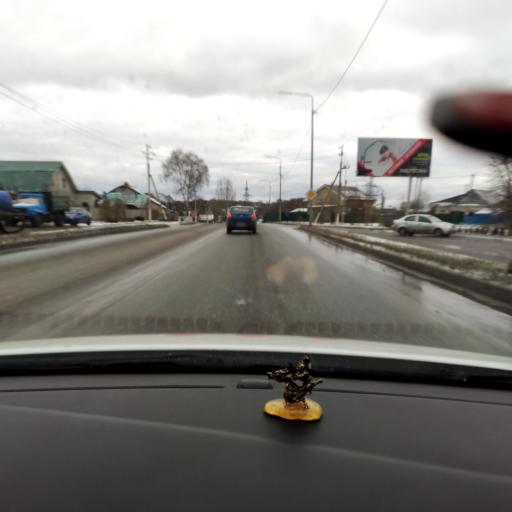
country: RU
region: Tatarstan
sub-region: Zelenodol'skiy Rayon
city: Zelenodolsk
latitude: 55.8475
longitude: 48.5350
